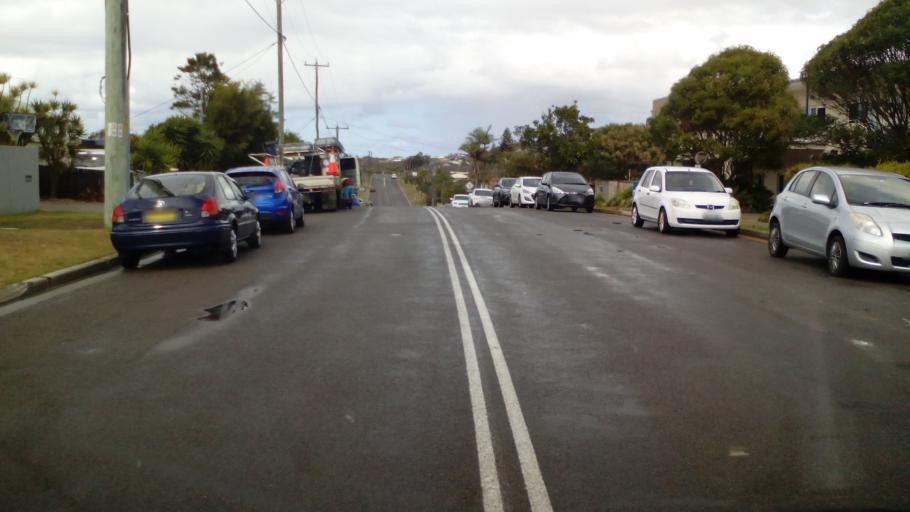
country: AU
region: New South Wales
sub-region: Lake Macquarie Shire
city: Belmont South
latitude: -33.1052
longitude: 151.6448
